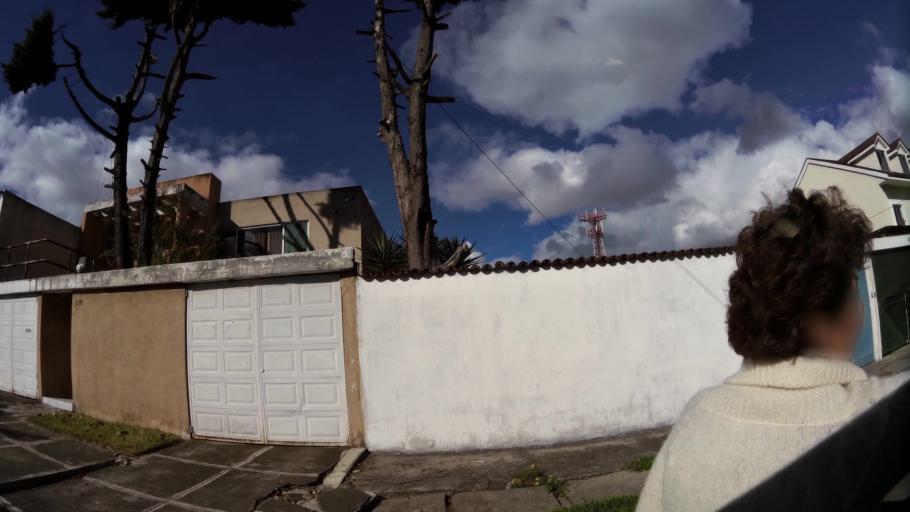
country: GT
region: Guatemala
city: Guatemala City
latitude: 14.6067
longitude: -90.5553
